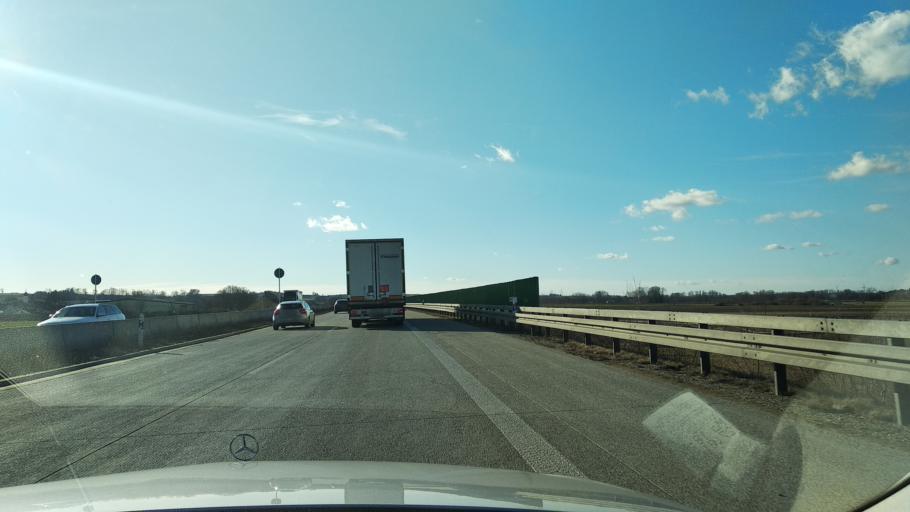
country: DE
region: Bavaria
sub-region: Upper Bavaria
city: Ampfing
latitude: 48.2509
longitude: 12.3865
